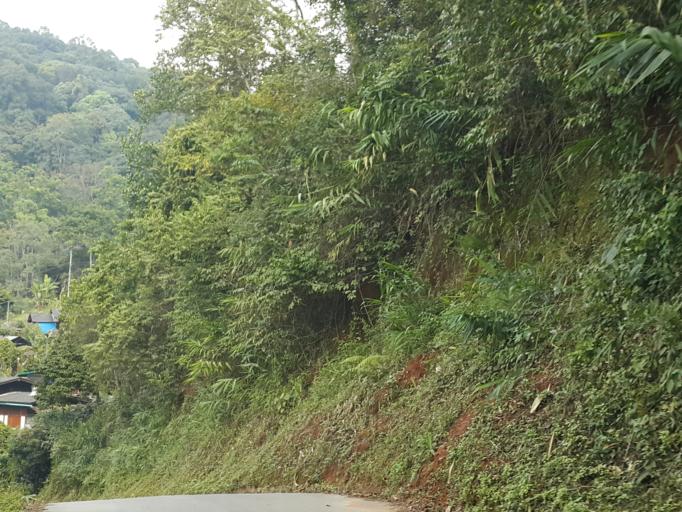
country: TH
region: Chiang Mai
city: Mae On
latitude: 18.8636
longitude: 99.3440
